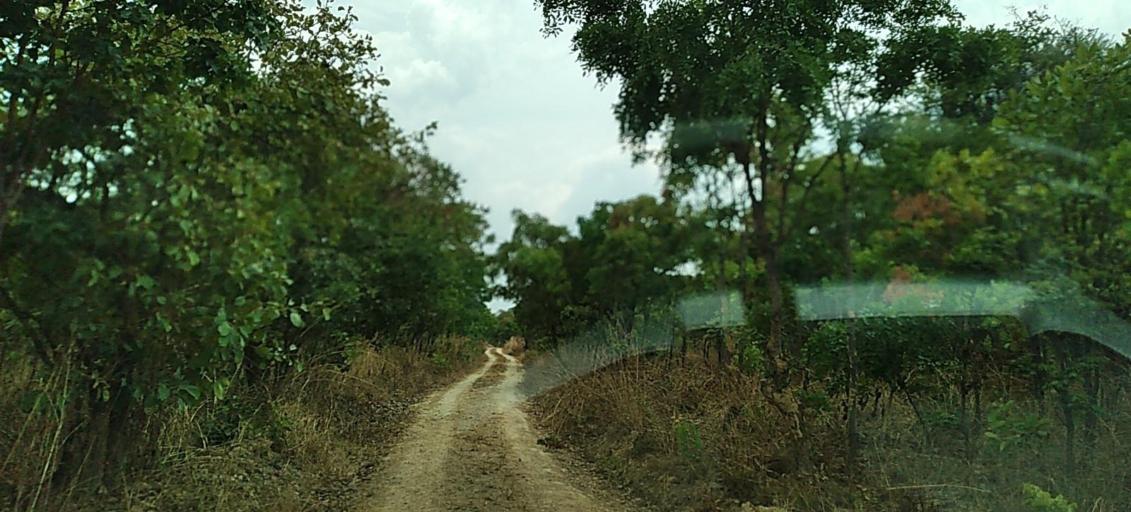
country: ZM
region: Copperbelt
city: Chililabombwe
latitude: -12.3224
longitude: 27.7862
